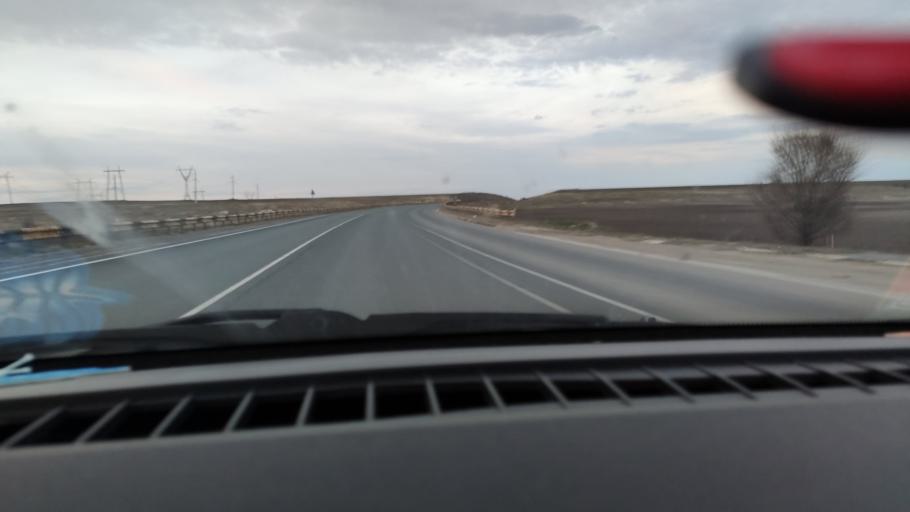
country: RU
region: Saratov
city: Sinodskoye
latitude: 51.9268
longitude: 46.5691
